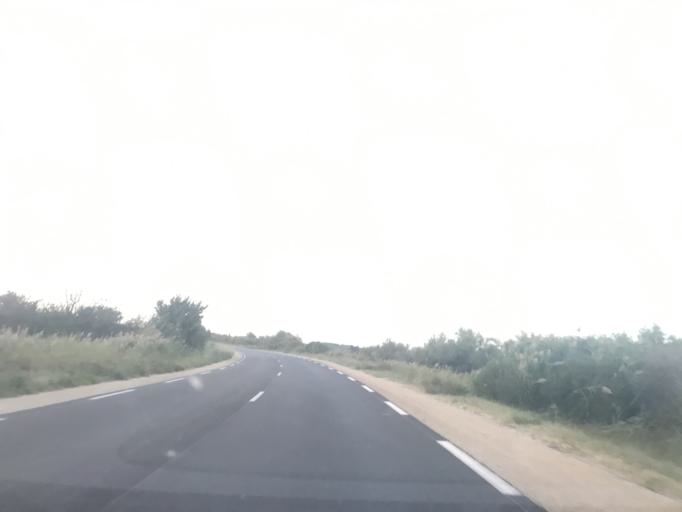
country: FR
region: Provence-Alpes-Cote d'Azur
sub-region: Departement des Bouches-du-Rhone
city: Saintes-Maries-de-la-Mer
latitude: 43.5400
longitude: 4.4010
